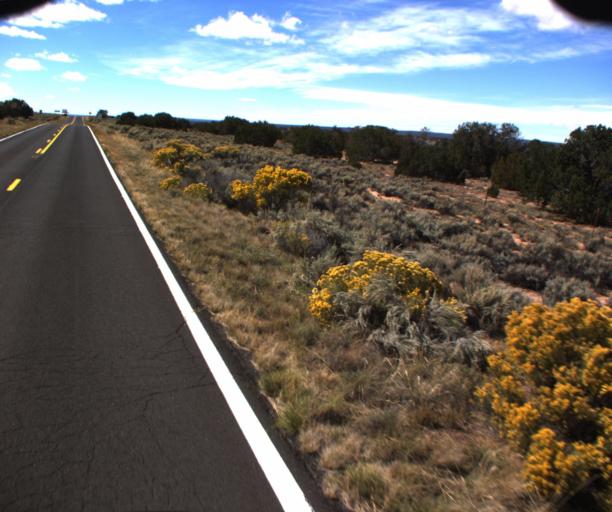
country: US
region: Arizona
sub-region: Apache County
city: Houck
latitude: 34.9054
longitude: -109.2327
